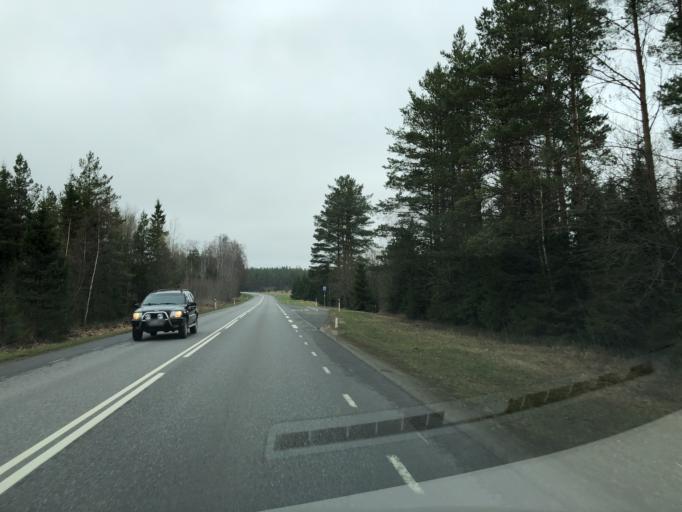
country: EE
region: Laeaene-Virumaa
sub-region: Rakke vald
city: Rakke
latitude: 59.0144
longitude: 26.2504
